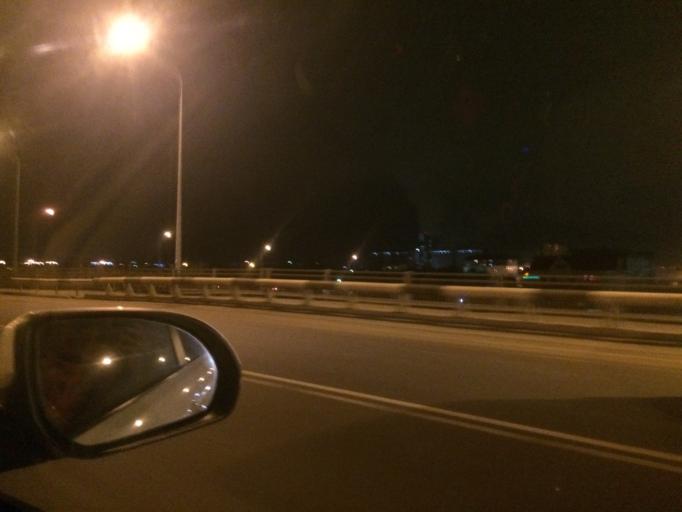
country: KZ
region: Astana Qalasy
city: Astana
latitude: 51.1844
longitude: 71.4465
